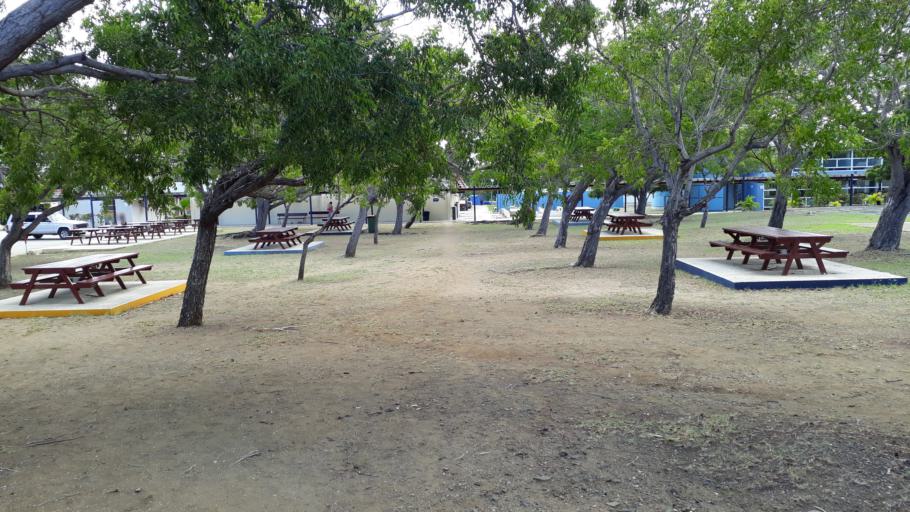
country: CW
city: Sint Michiel Liber
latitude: 12.1575
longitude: -68.9611
